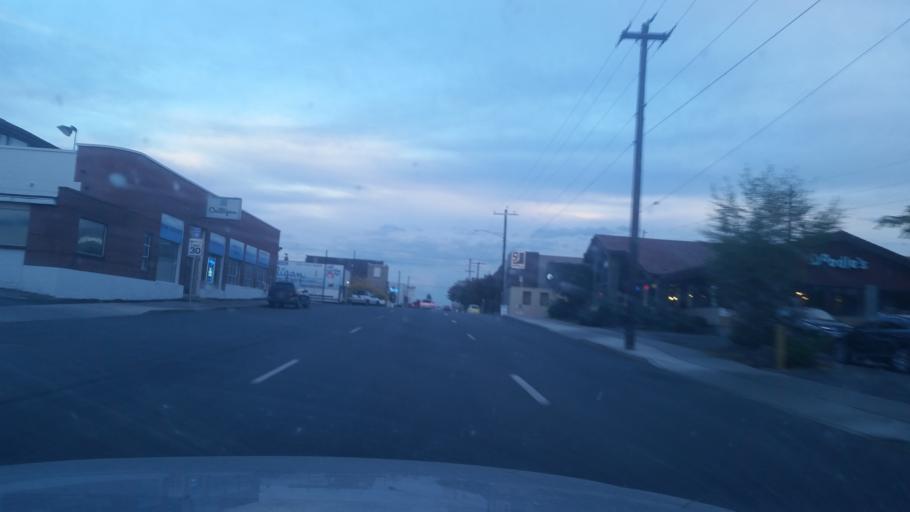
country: US
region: Washington
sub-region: Spokane County
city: Spokane
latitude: 47.6536
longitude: -117.4108
